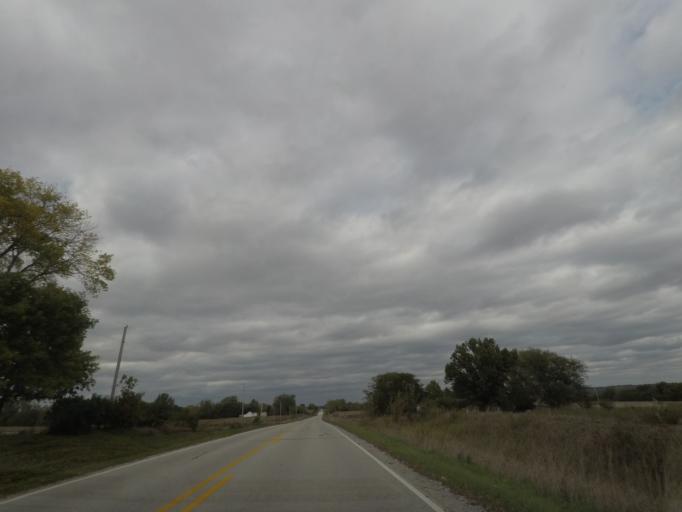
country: US
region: Iowa
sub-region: Story County
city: Huxley
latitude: 41.8619
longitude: -93.5317
